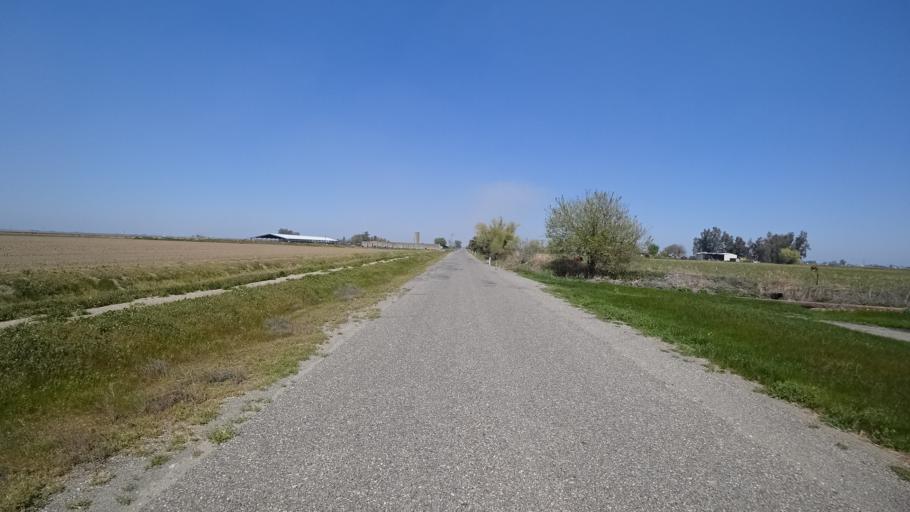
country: US
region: California
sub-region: Glenn County
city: Willows
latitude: 39.5486
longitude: -122.1028
